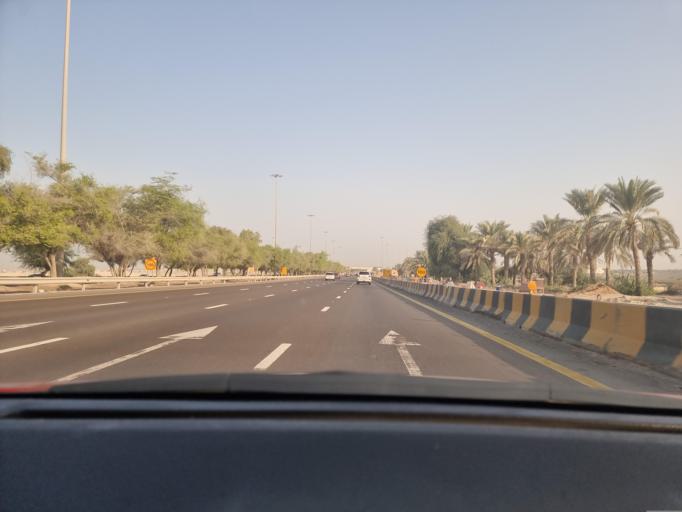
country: AE
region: Abu Dhabi
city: Abu Dhabi
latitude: 24.4584
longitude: 54.6783
